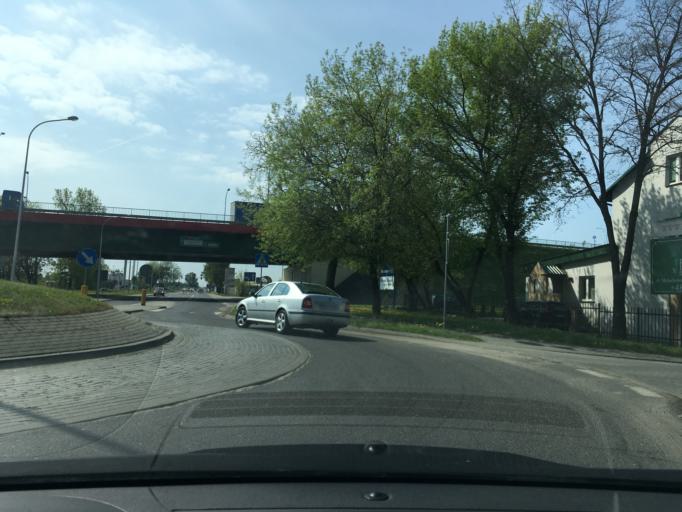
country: PL
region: Lublin Voivodeship
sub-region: Powiat pulawski
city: Pulawy
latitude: 51.4384
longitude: 21.9481
